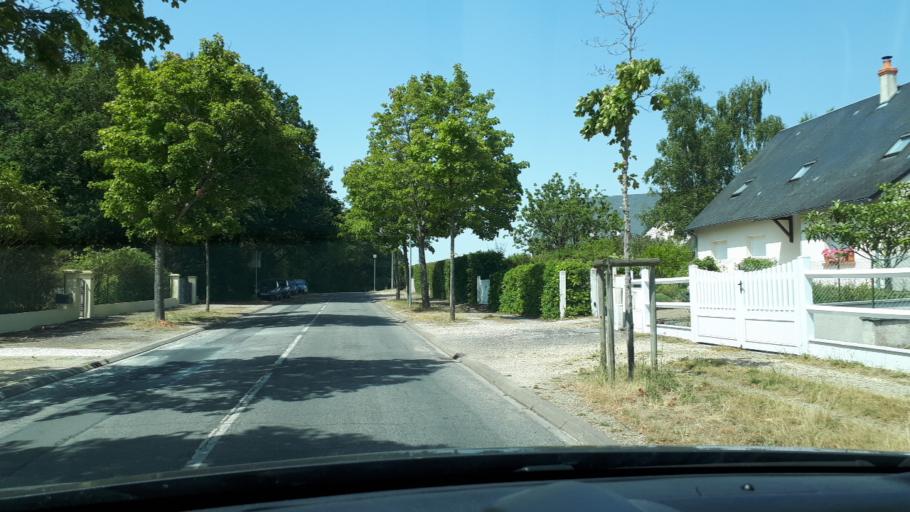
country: FR
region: Centre
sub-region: Departement du Loir-et-Cher
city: Vendome
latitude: 47.8150
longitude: 1.0474
